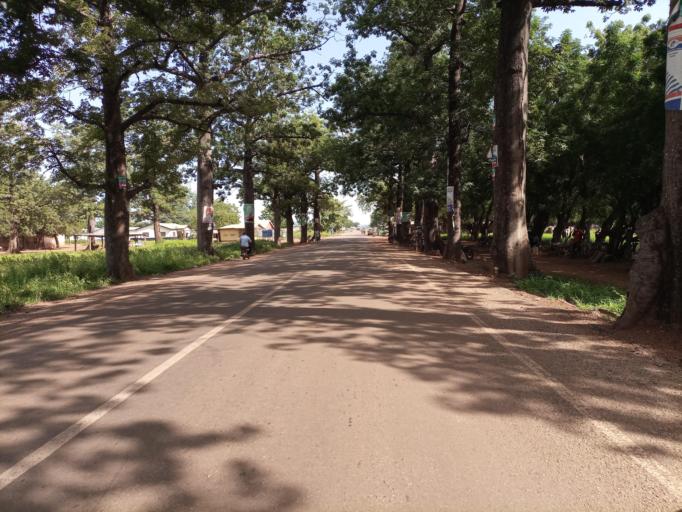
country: GH
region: Northern
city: Savelugu
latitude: 9.5560
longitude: -0.9462
